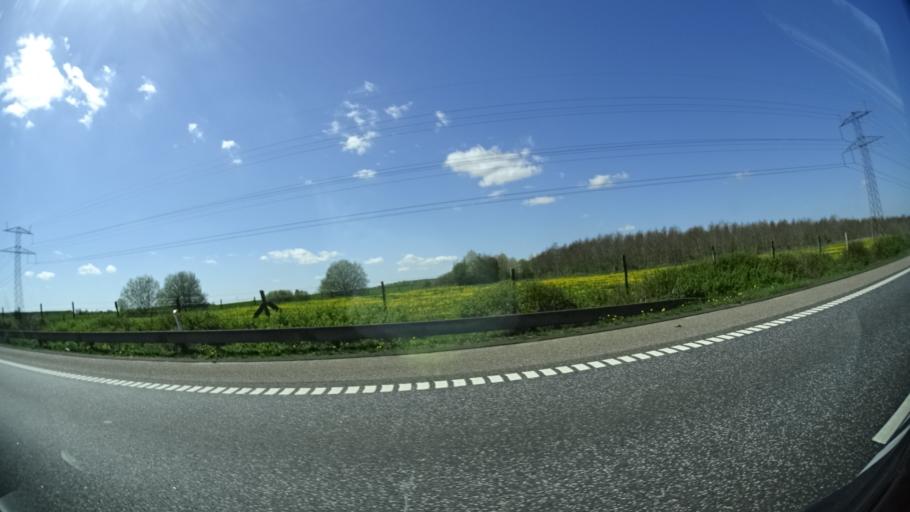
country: DK
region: Central Jutland
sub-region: Arhus Kommune
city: Trige
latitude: 56.2454
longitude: 10.1241
